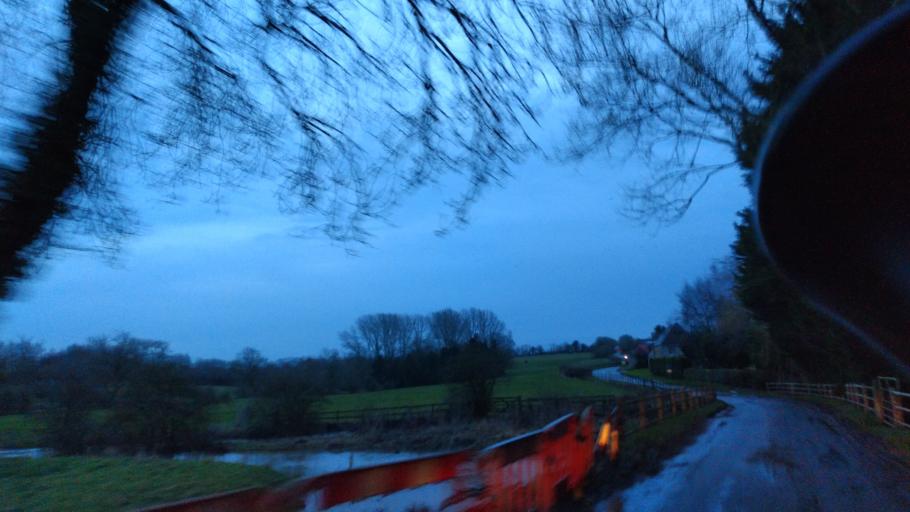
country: GB
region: England
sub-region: Oxfordshire
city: Shrivenham
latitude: 51.6136
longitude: -1.6809
